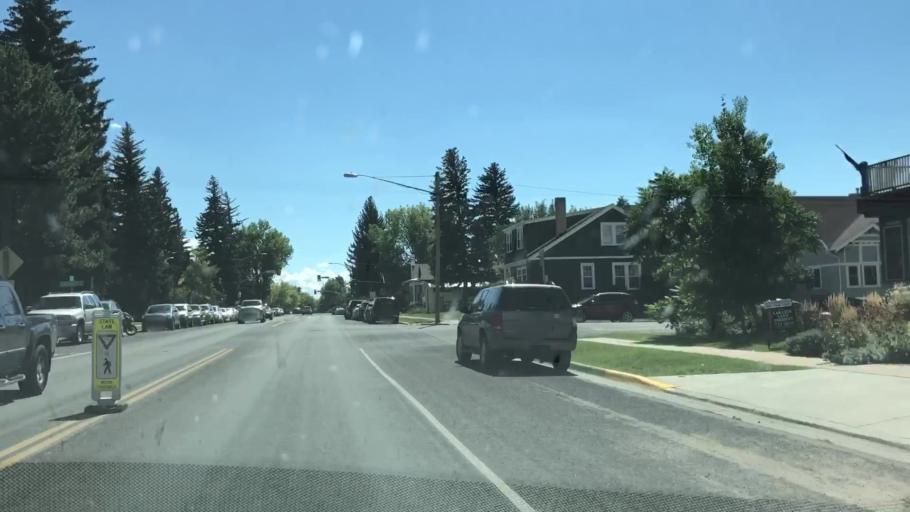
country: US
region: Wyoming
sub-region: Albany County
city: Laramie
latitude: 41.3128
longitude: -105.5855
